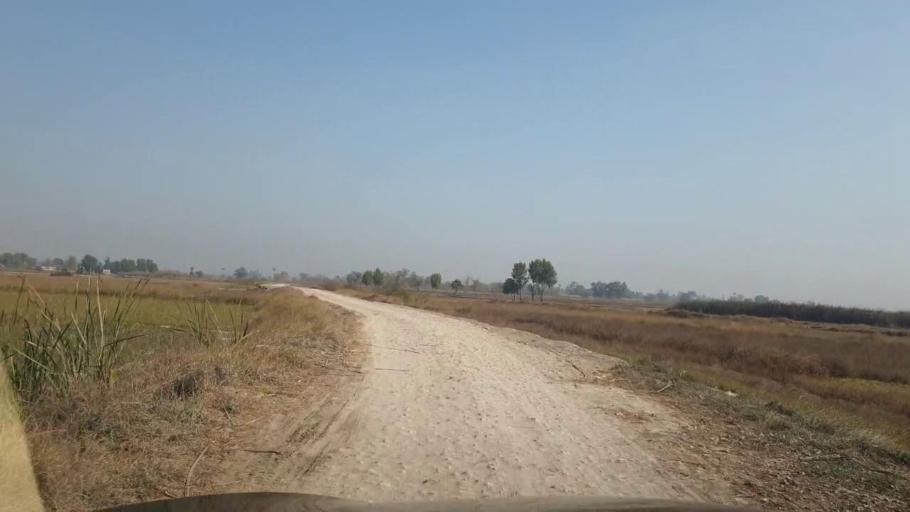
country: PK
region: Sindh
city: Ubauro
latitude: 28.1435
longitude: 69.7527
